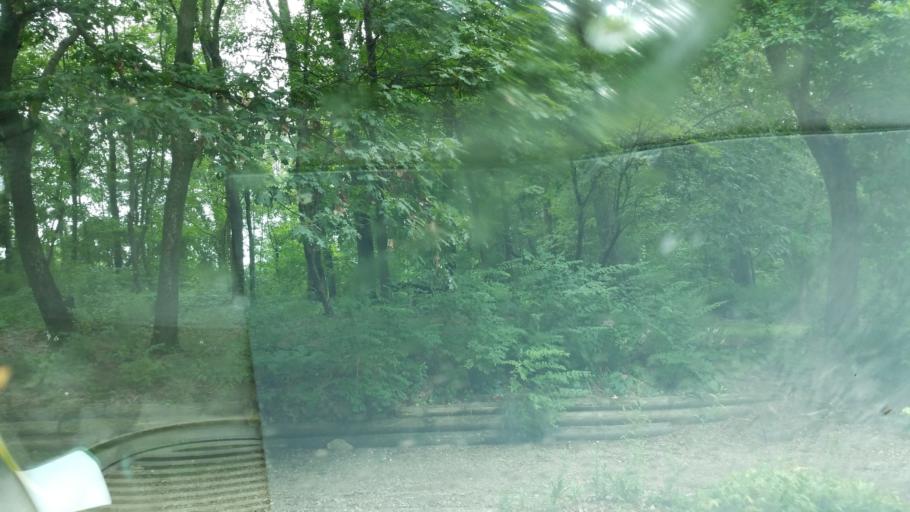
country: US
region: Ohio
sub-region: Sandusky County
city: Bellville
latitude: 40.5807
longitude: -82.4587
